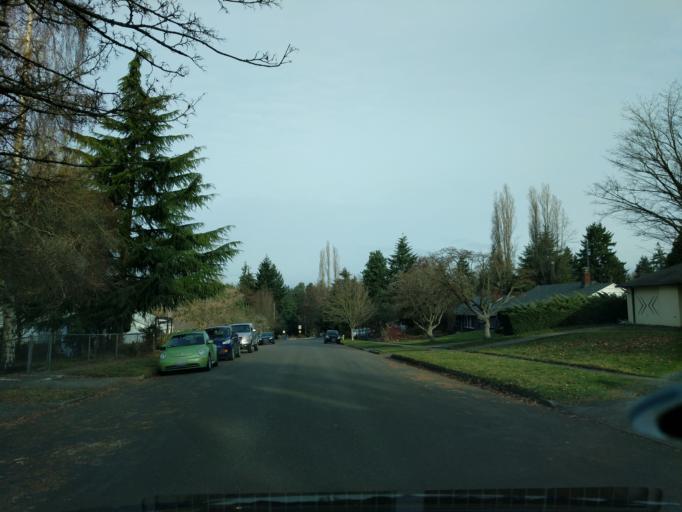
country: US
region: Washington
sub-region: King County
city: Shoreline
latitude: 47.7539
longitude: -122.3267
